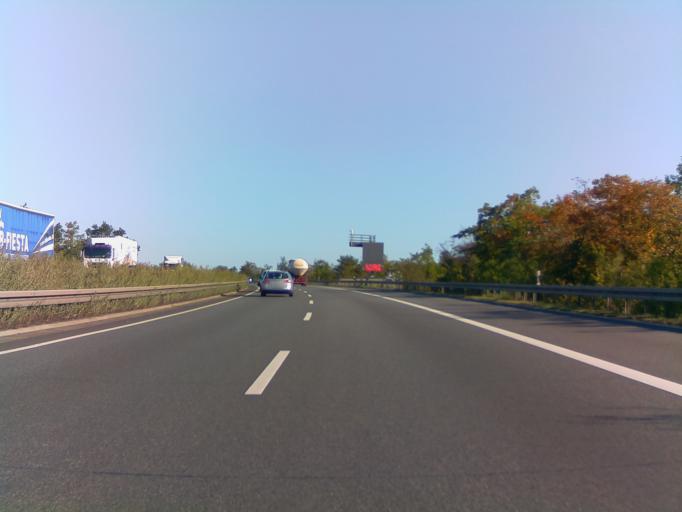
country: DE
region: Hesse
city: Pfungstadt
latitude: 49.8276
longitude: 8.6336
